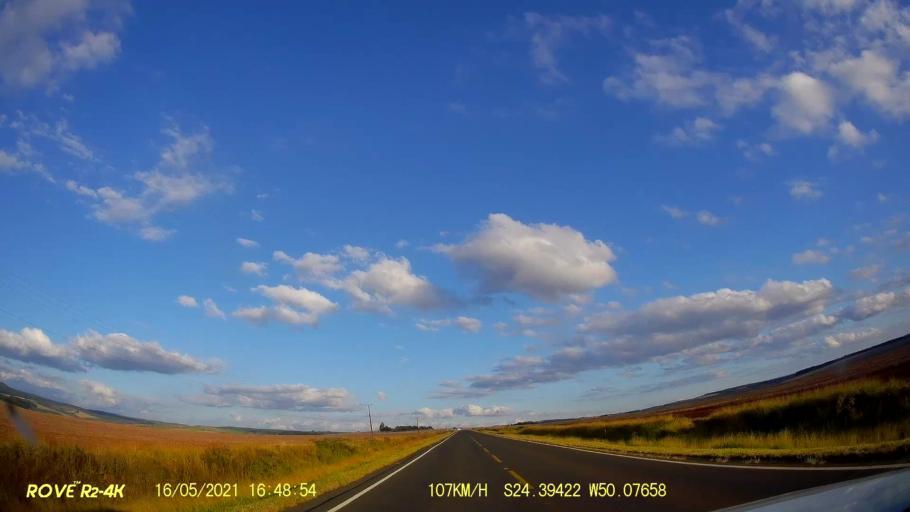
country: BR
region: Parana
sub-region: Pirai Do Sul
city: Pirai do Sul
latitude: -24.3945
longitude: -50.0764
